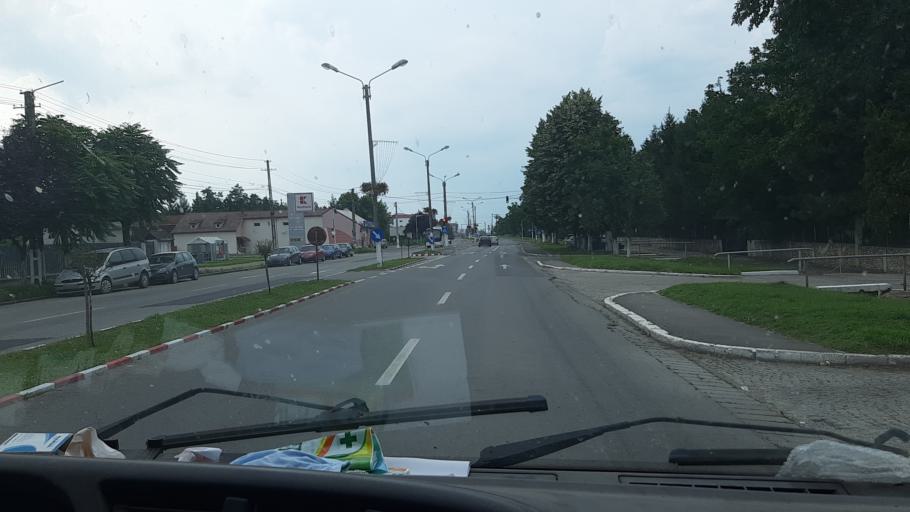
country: RO
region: Timis
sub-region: Municipiul Lugoj
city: Lugoj
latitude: 45.6992
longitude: 21.8954
